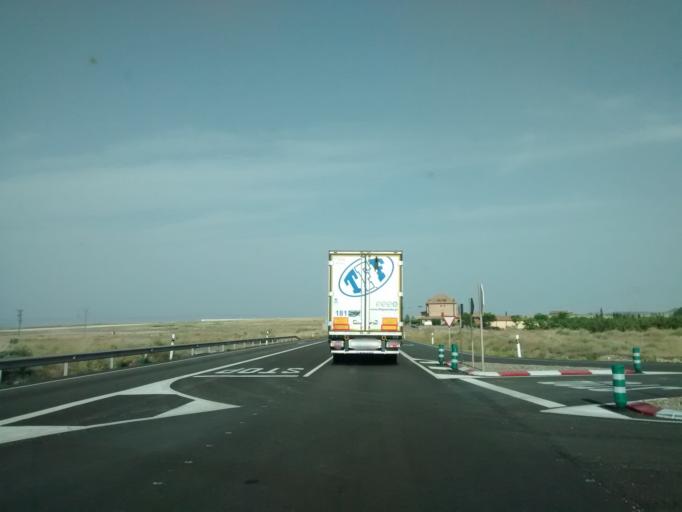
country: ES
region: Aragon
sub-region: Provincia de Zaragoza
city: Albeta
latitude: 41.8310
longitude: -1.5037
